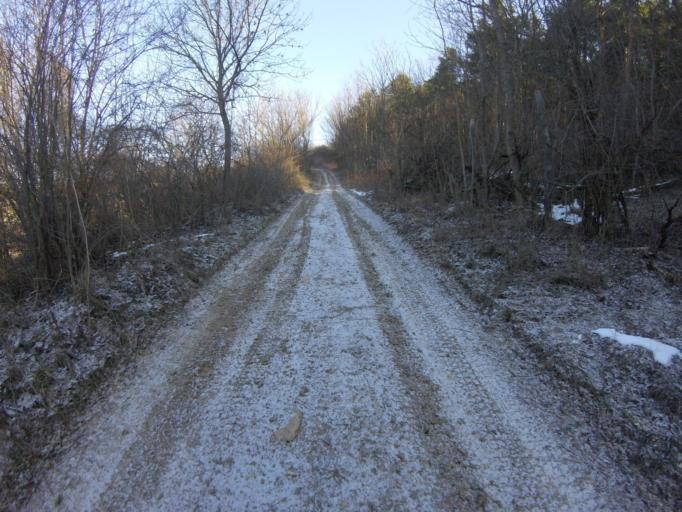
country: HU
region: Komarom-Esztergom
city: Piliscsev
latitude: 47.6710
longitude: 18.8310
